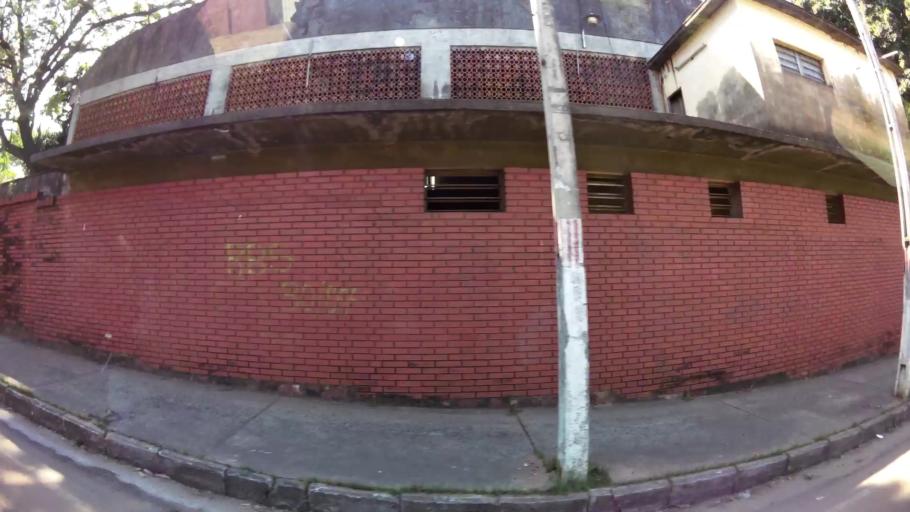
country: PY
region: Central
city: San Lorenzo
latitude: -25.3510
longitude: -57.5043
